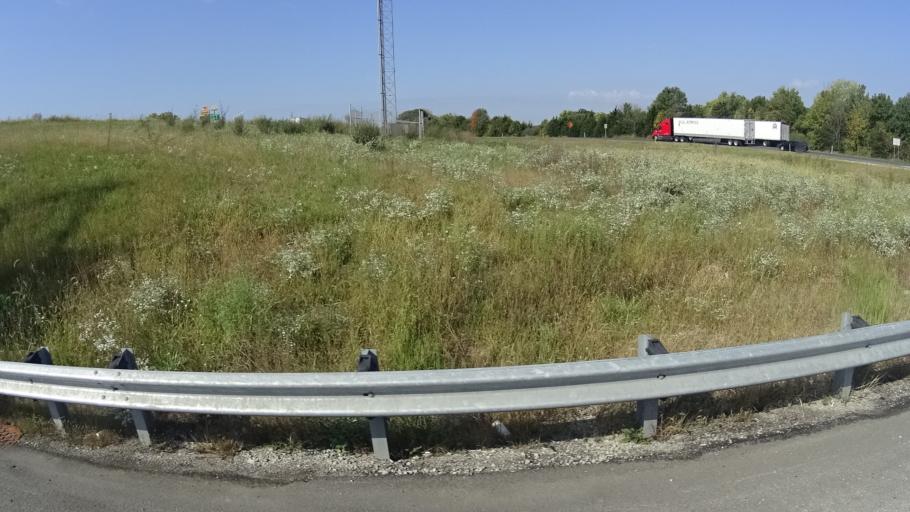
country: US
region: Indiana
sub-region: Madison County
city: Ingalls
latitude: 39.9943
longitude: -85.8432
